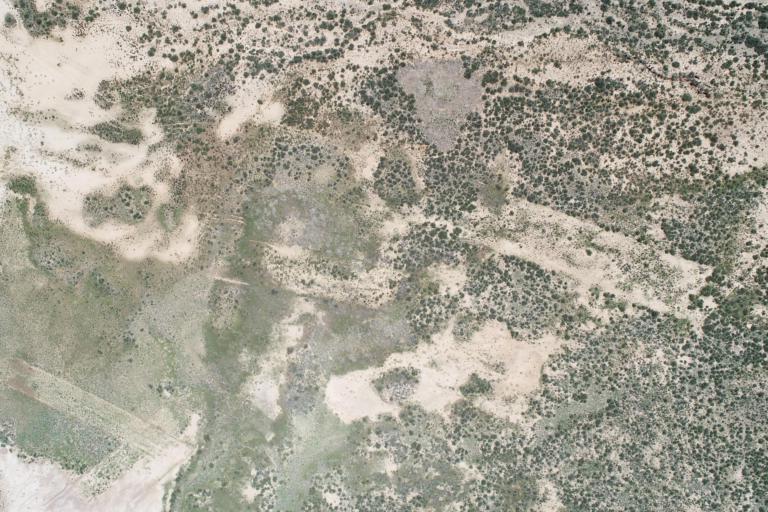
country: BO
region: La Paz
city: Curahuara de Carangas
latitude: -17.3183
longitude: -68.4972
